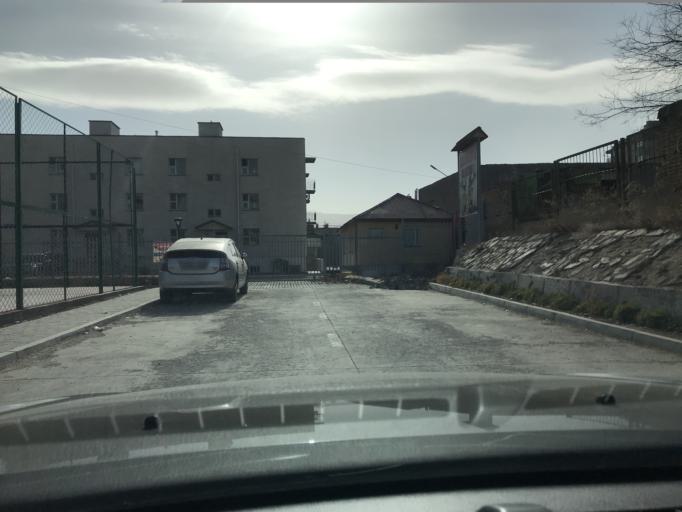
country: MN
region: Ulaanbaatar
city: Ulaanbaatar
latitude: 47.9205
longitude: 106.9516
